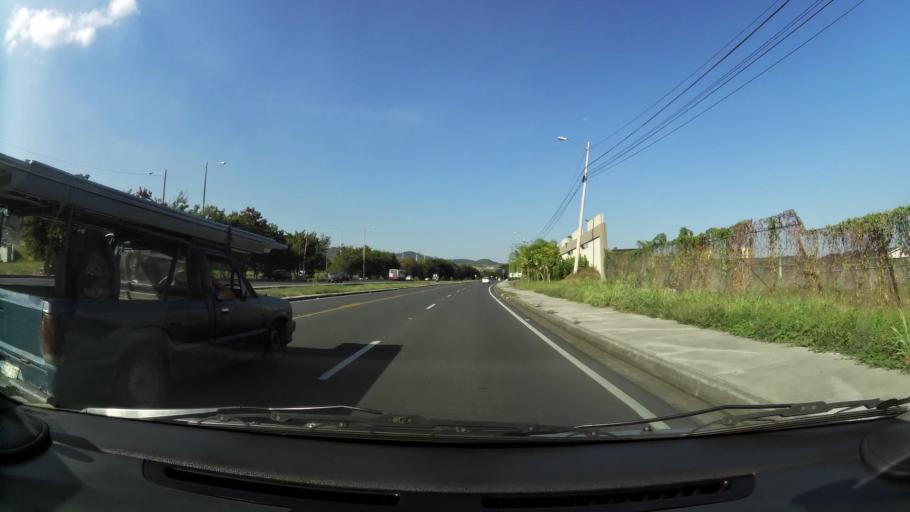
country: EC
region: Guayas
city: Santa Lucia
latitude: -2.1832
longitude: -79.9951
